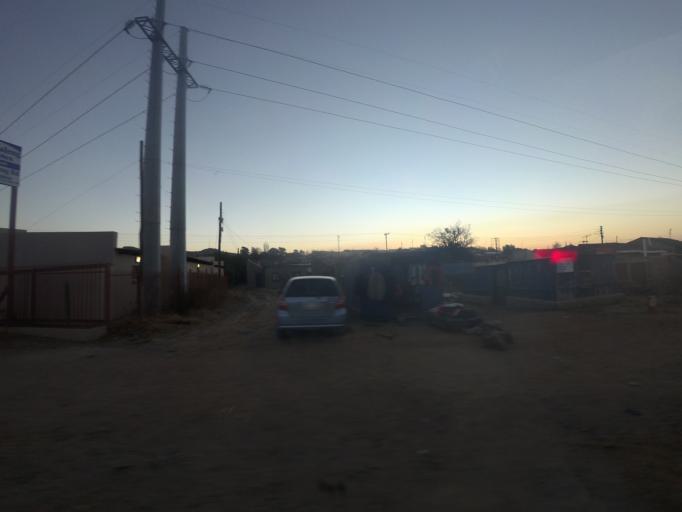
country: LS
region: Maseru
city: Maseru
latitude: -29.3144
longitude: 27.5107
